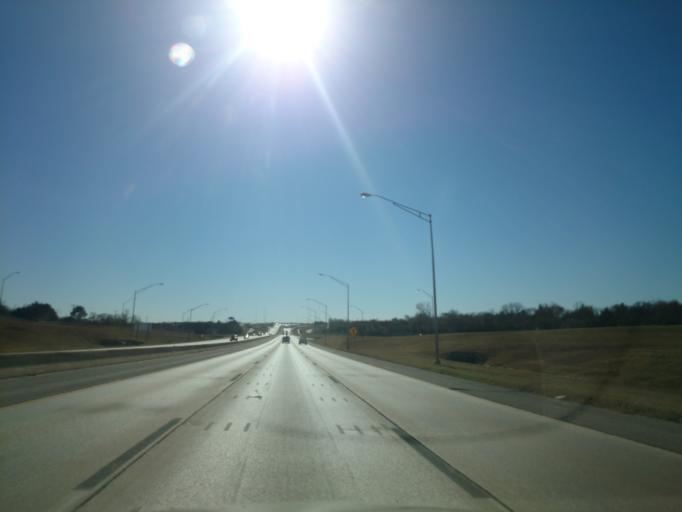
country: US
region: Oklahoma
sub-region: Oklahoma County
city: Edmond
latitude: 35.6232
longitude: -97.4250
